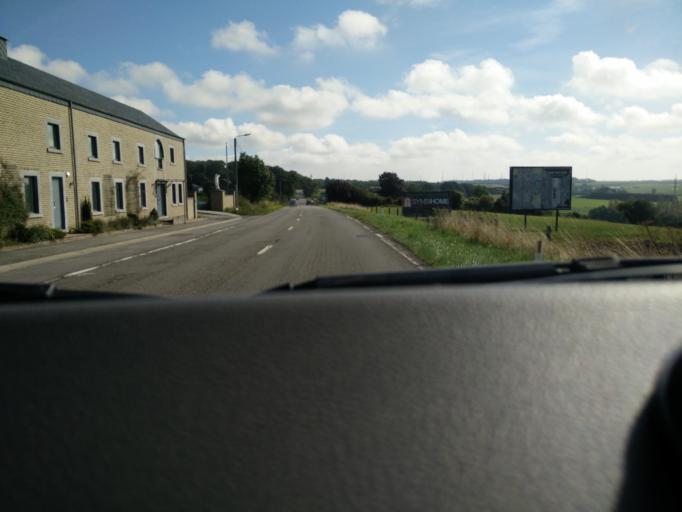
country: BE
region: Wallonia
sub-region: Province de Namur
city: Houyet
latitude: 50.2614
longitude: 5.0123
